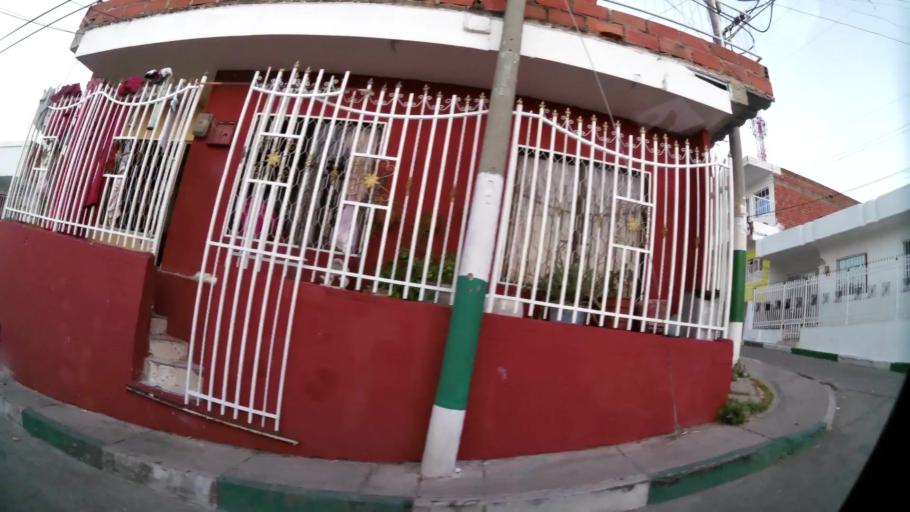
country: CO
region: Bolivar
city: Cartagena
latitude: 10.4020
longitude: -75.5134
